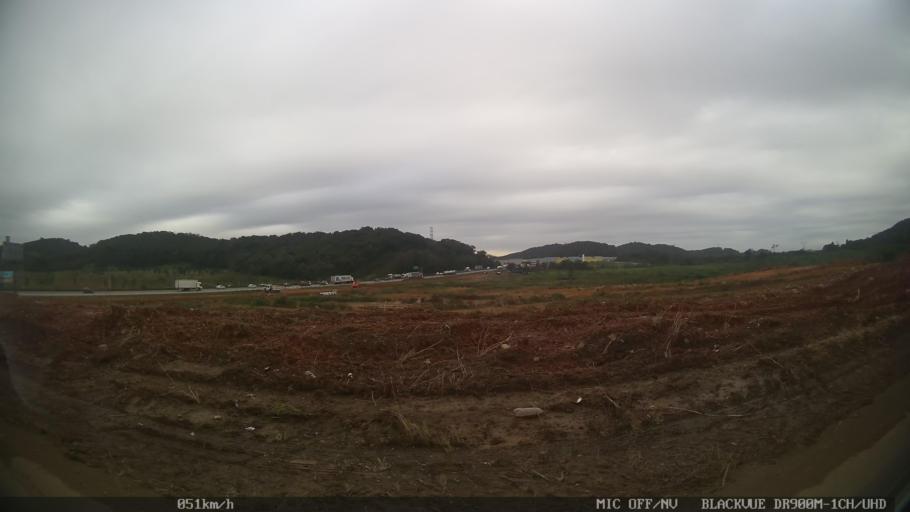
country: BR
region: Santa Catarina
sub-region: Joinville
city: Joinville
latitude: -26.2512
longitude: -48.9098
